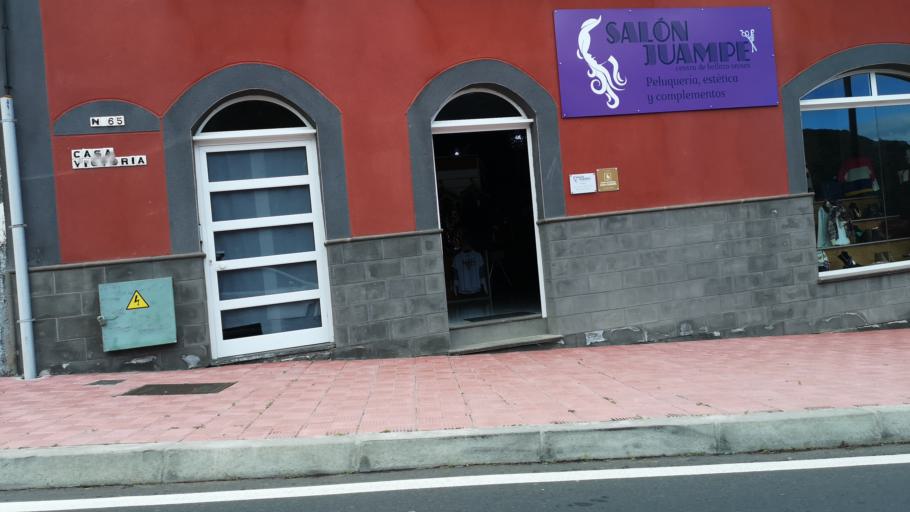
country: ES
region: Canary Islands
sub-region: Provincia de Santa Cruz de Tenerife
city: Hermigua
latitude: 28.1558
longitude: -17.1977
